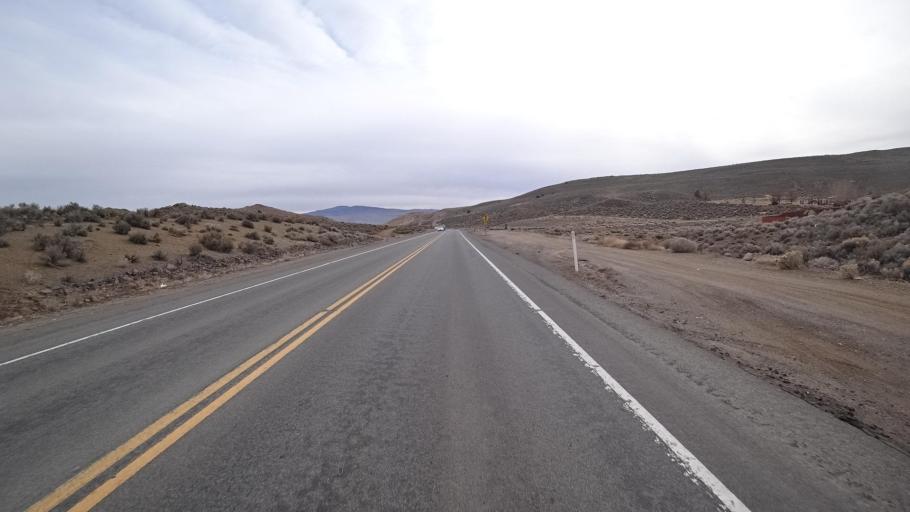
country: US
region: Nevada
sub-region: Washoe County
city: Sun Valley
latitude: 39.6073
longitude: -119.7536
